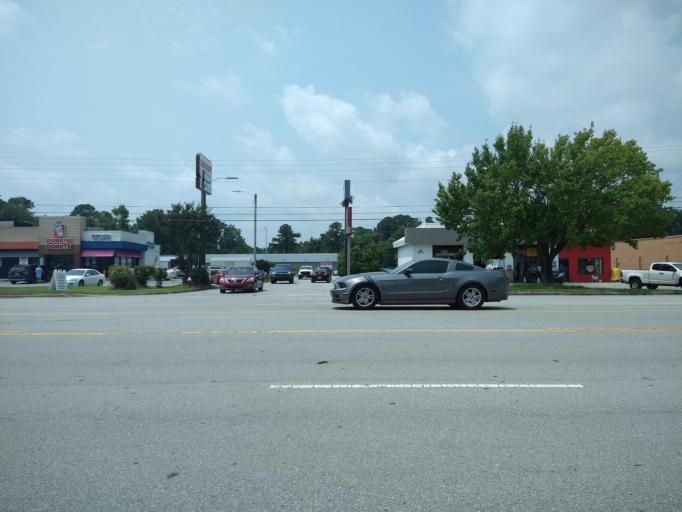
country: US
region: North Carolina
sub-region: Onslow County
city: Pumpkin Center
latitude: 34.7718
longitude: -77.3872
